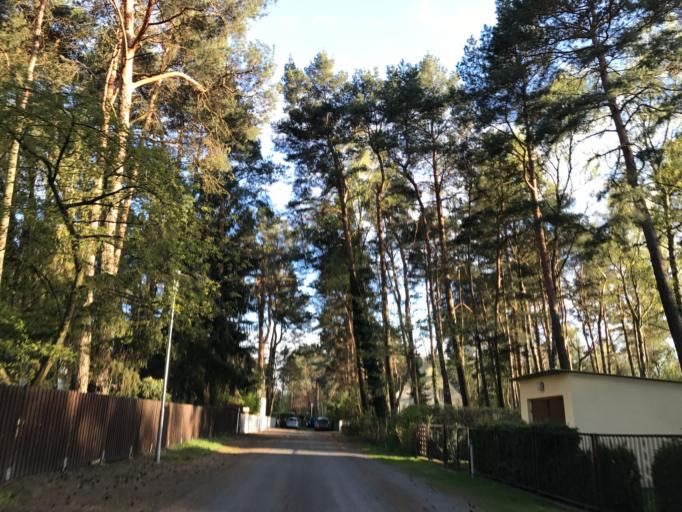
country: DE
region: Berlin
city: Kladow
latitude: 52.4670
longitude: 13.0987
